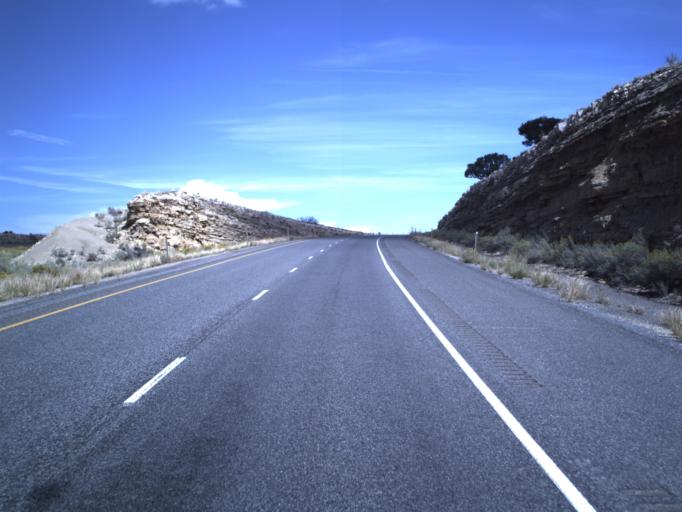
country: US
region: Utah
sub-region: Emery County
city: Castle Dale
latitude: 38.8899
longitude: -110.6439
